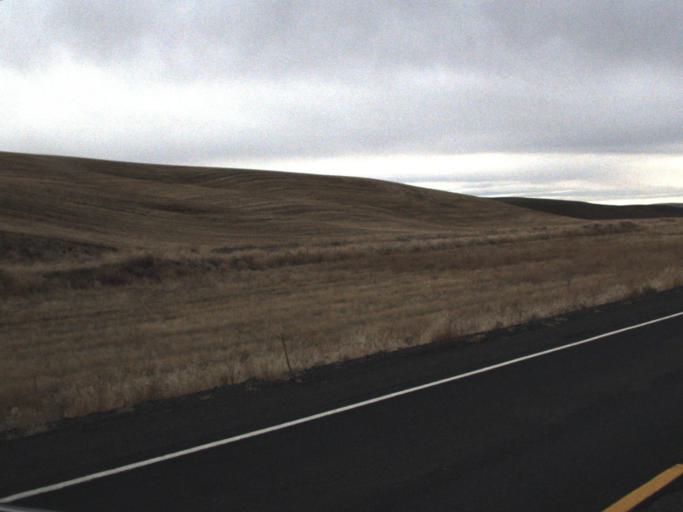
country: US
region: Washington
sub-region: Garfield County
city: Pomeroy
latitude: 46.7966
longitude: -117.8744
